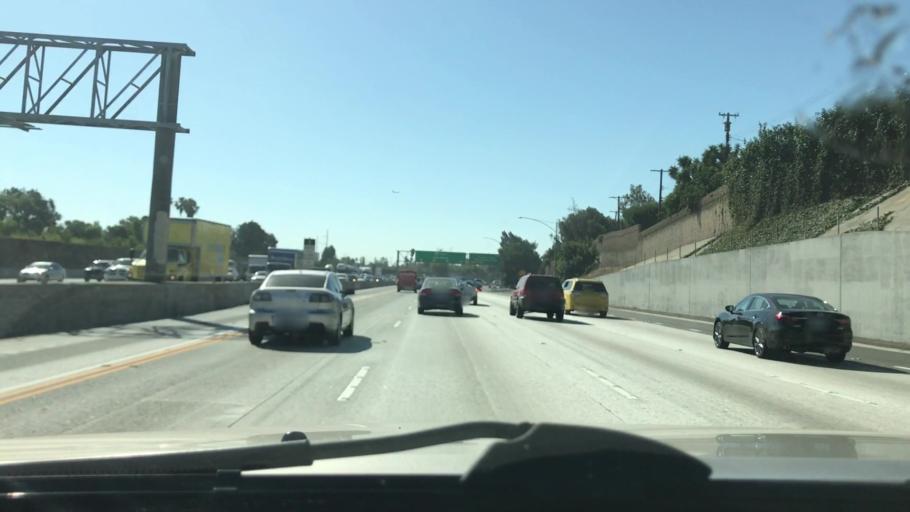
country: US
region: California
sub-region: Los Angeles County
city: Ladera Heights
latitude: 33.9704
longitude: -118.3760
